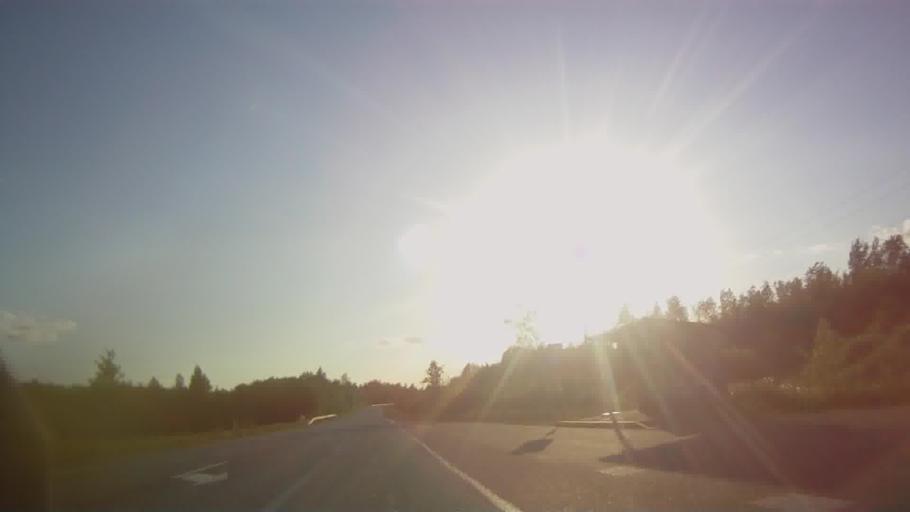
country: LV
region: Livani
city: Livani
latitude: 56.5239
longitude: 26.4227
